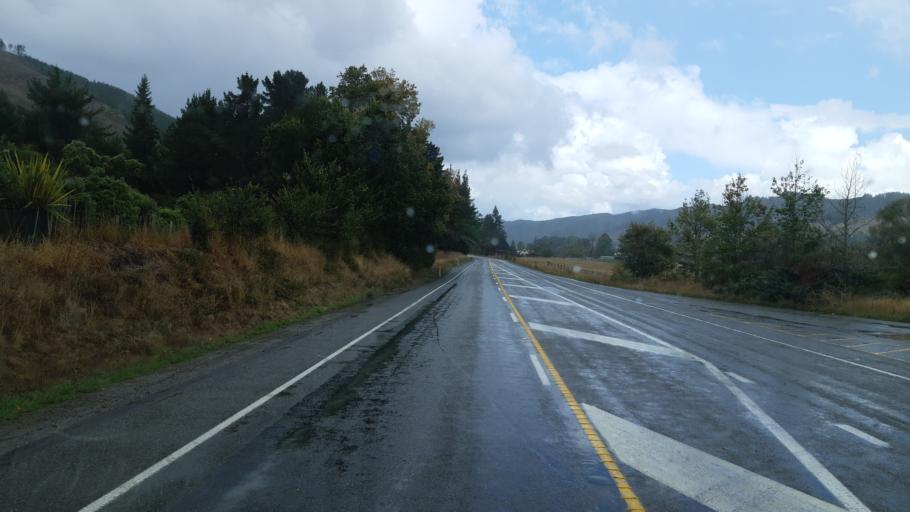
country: NZ
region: Tasman
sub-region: Tasman District
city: Wakefield
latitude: -41.4519
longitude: 172.8363
